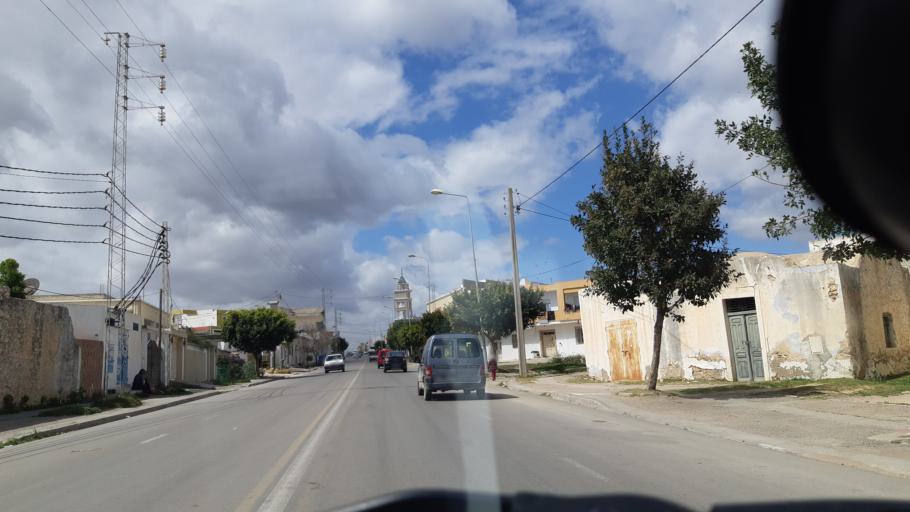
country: TN
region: Susah
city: Akouda
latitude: 35.8776
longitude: 10.5312
